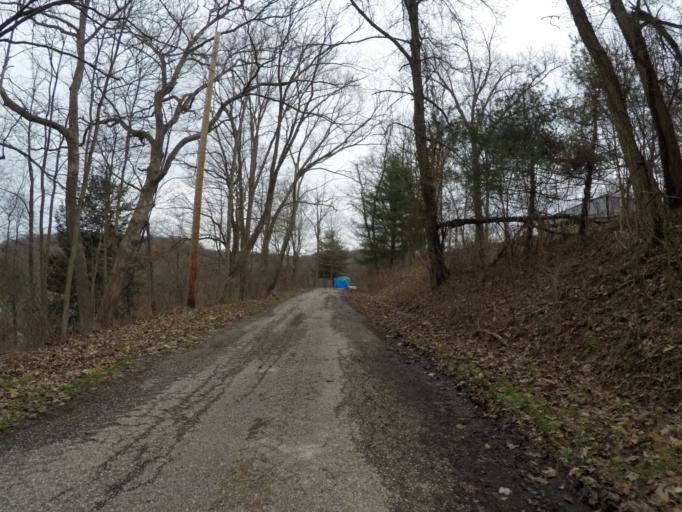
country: US
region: Ohio
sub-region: Lawrence County
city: Burlington
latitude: 38.3919
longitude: -82.5191
